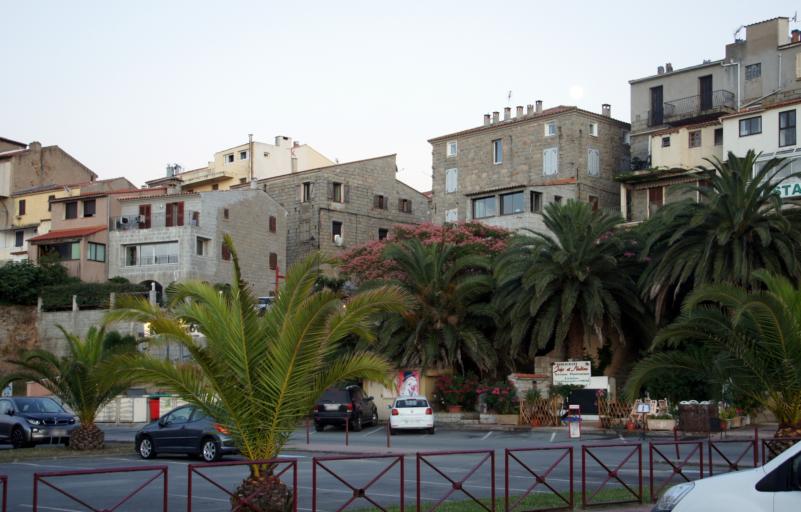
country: FR
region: Corsica
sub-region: Departement de la Corse-du-Sud
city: Propriano
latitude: 41.6765
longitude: 8.9036
